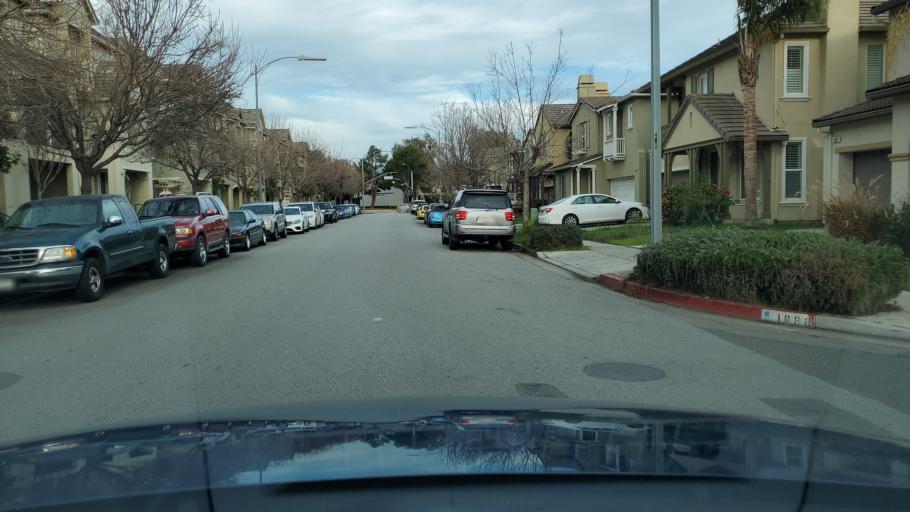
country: US
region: California
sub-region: Santa Clara County
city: Milpitas
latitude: 37.3930
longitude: -121.9030
